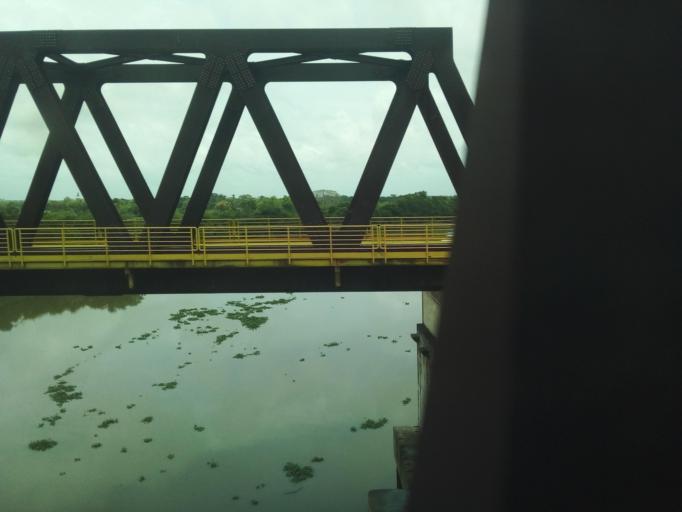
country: BR
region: Maranhao
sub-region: Vitoria Do Mearim
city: Vitoria do Mearim
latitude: -3.5467
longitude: -44.8319
